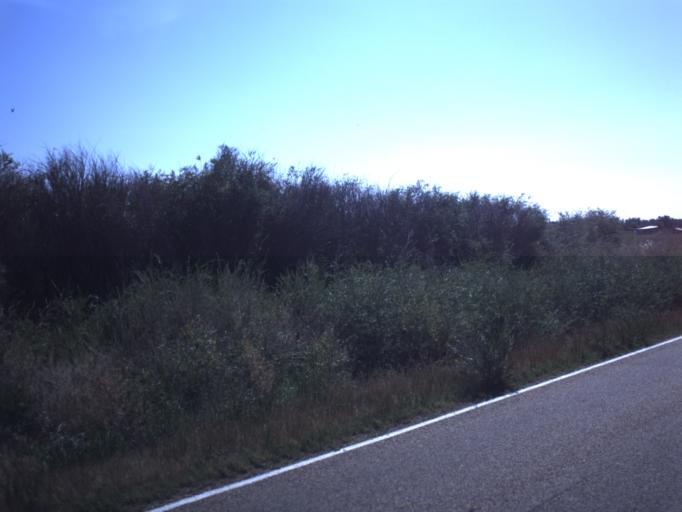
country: US
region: Utah
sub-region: Duchesne County
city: Duchesne
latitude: 40.3314
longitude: -110.2713
